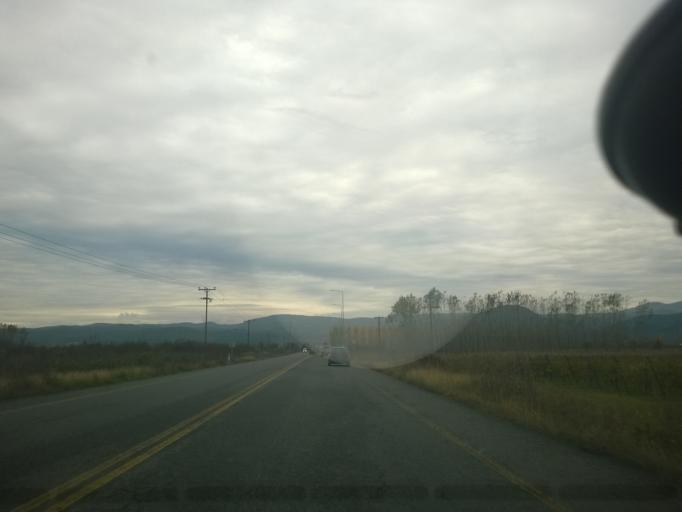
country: GR
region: Central Macedonia
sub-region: Nomos Pellis
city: Apsalos
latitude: 40.9177
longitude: 22.0770
